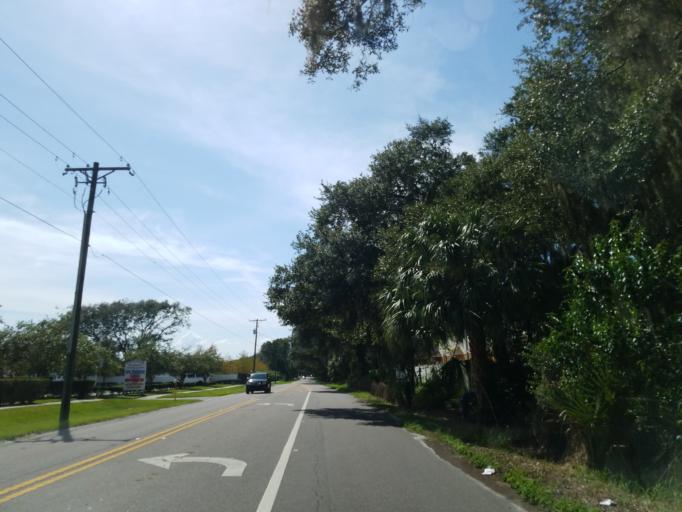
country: US
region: Florida
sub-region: Hillsborough County
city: Riverview
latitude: 27.8790
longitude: -82.3228
